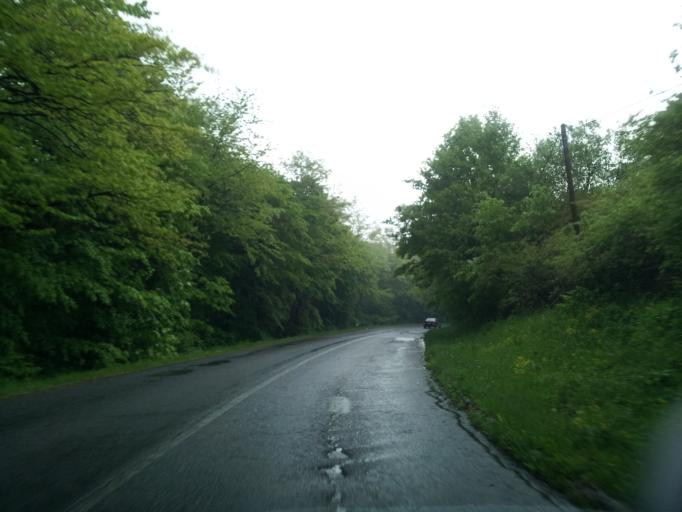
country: HU
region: Baranya
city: Hosszuheteny
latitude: 46.1718
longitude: 18.3248
